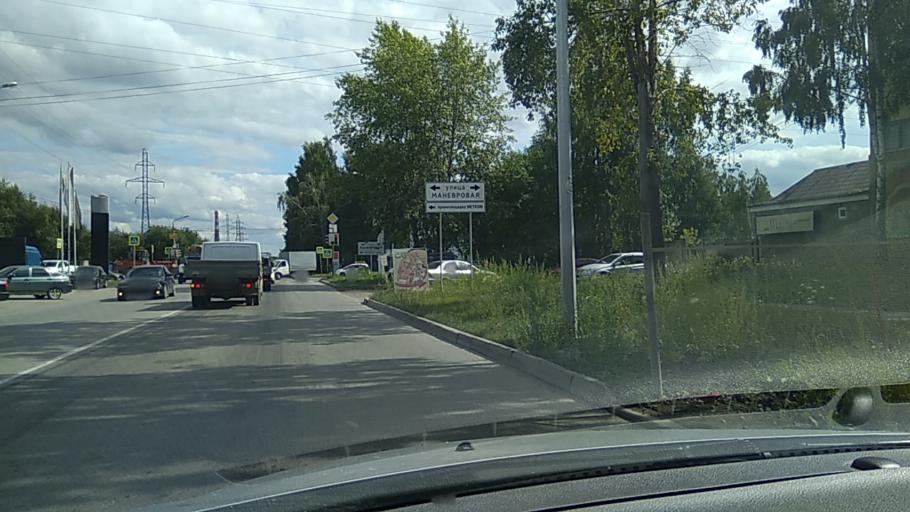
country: RU
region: Sverdlovsk
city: Shuvakish
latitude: 56.8851
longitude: 60.5319
